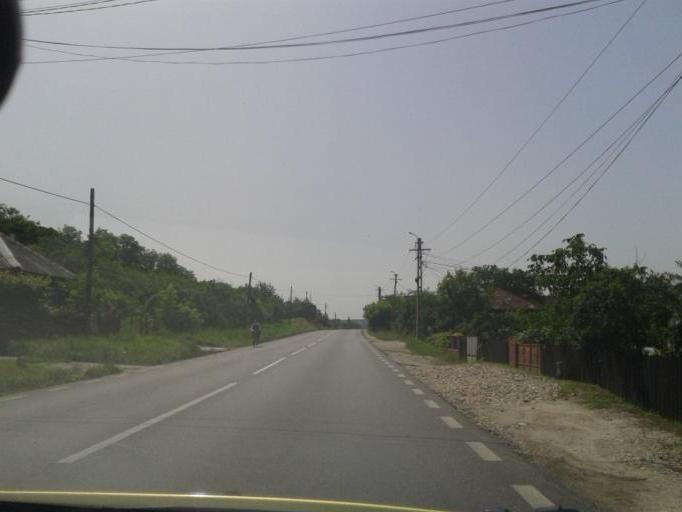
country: RO
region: Arges
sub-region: Comuna Babana
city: Babana
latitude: 44.9048
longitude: 24.7302
